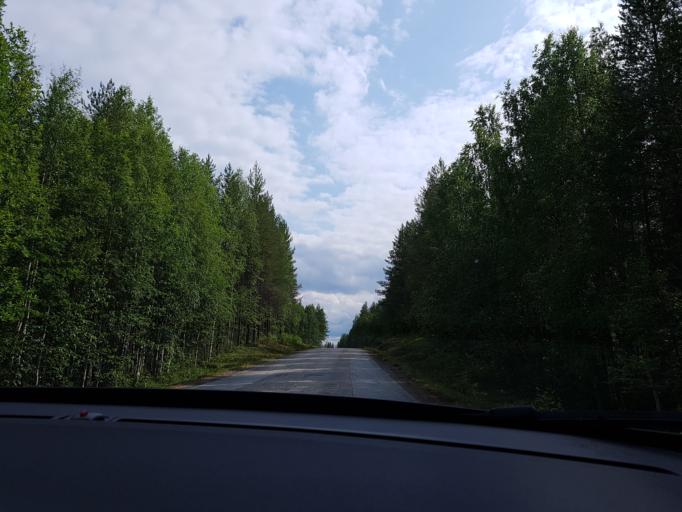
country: FI
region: Kainuu
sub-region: Kehys-Kainuu
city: Kuhmo
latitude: 64.3996
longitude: 29.7765
